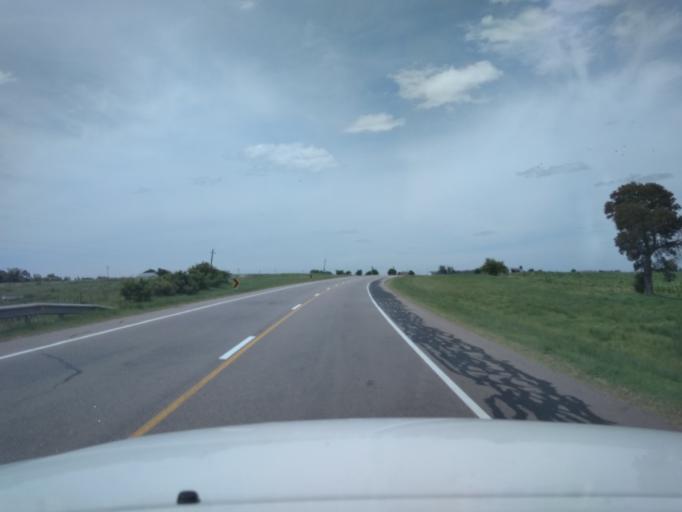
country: UY
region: Florida
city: Cardal
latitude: -34.3179
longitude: -56.2422
